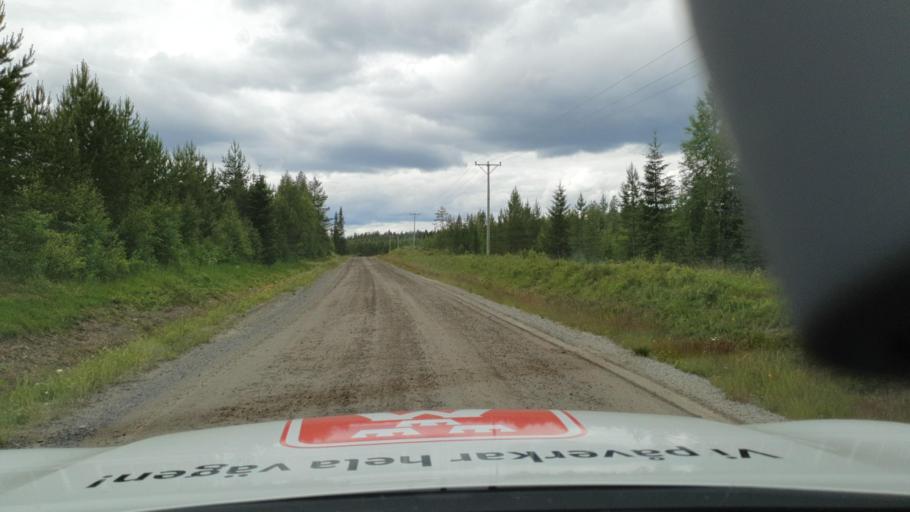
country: SE
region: Vaesterbotten
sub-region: Bjurholms Kommun
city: Bjurholm
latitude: 63.8085
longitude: 19.0717
